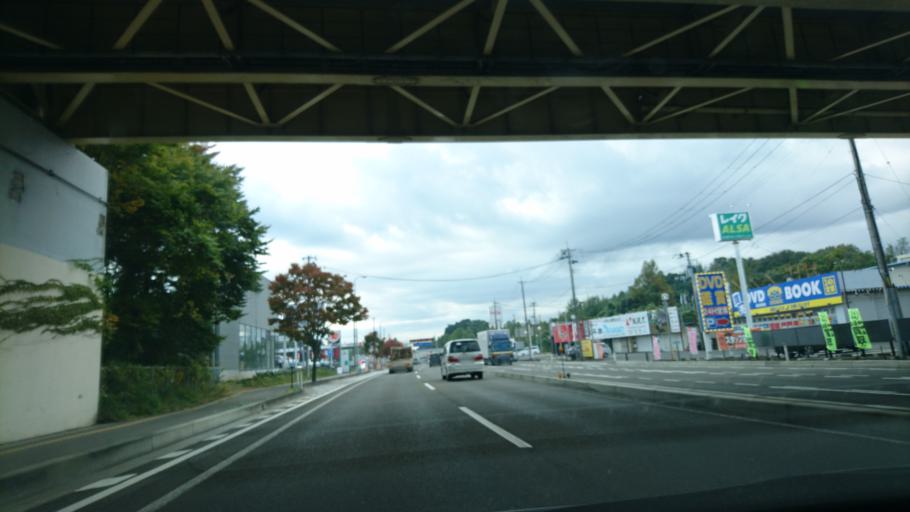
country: JP
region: Miyagi
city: Tomiya
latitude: 38.3486
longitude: 140.8765
